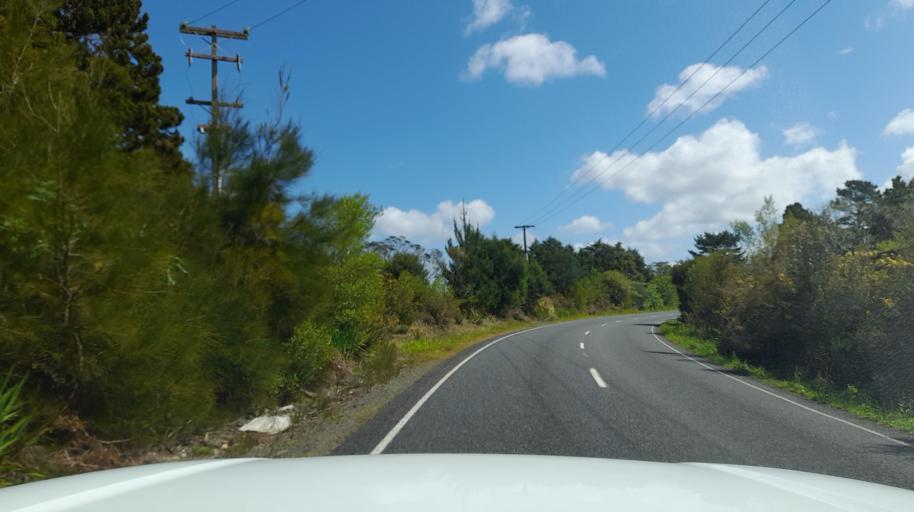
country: NZ
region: Northland
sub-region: Far North District
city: Kerikeri
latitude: -35.2415
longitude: 173.8873
